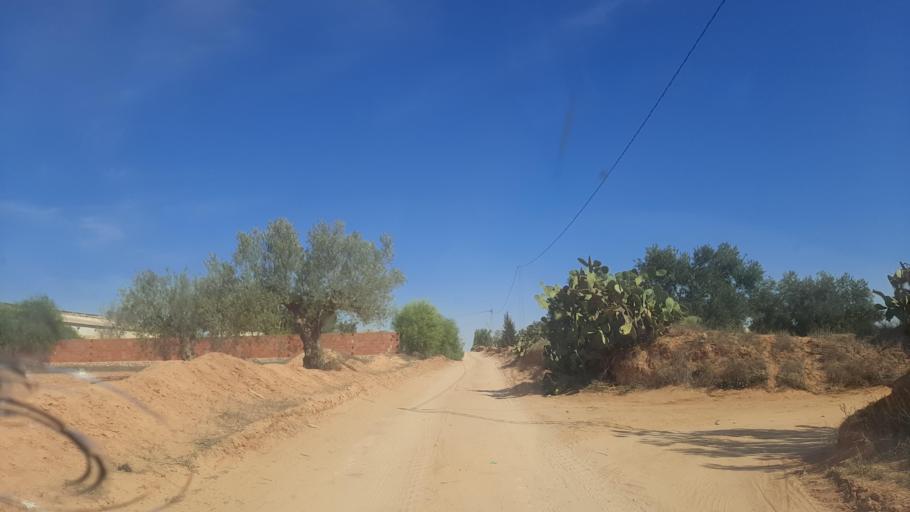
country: TN
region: Safaqis
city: Sfax
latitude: 34.8769
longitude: 10.5696
